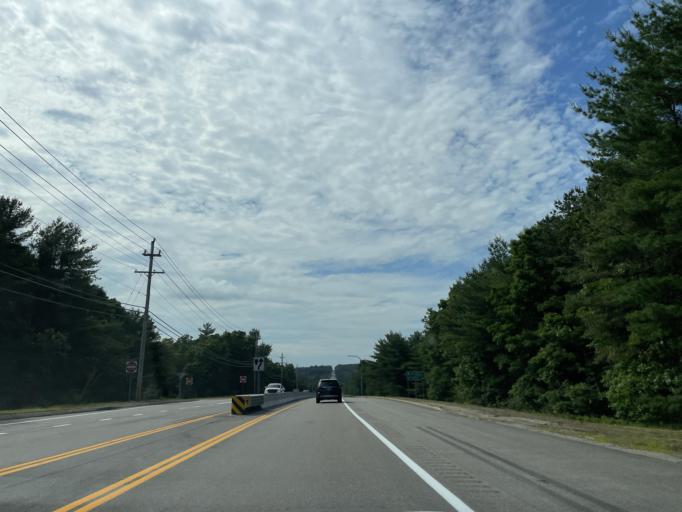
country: US
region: Rhode Island
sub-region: Kent County
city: West Greenwich
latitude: 41.5992
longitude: -71.6534
